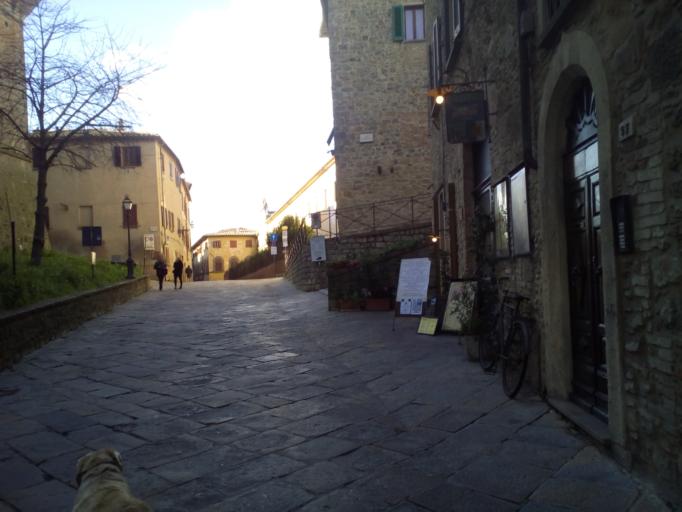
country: IT
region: Tuscany
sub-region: Province of Pisa
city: Volterra
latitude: 43.3999
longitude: 10.8690
